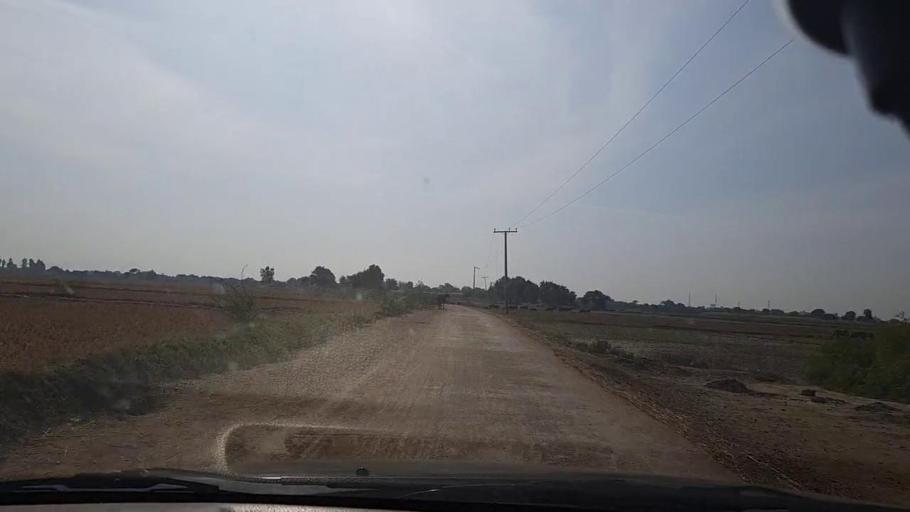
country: PK
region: Sindh
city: Mirpur Batoro
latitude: 24.7417
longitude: 68.2708
